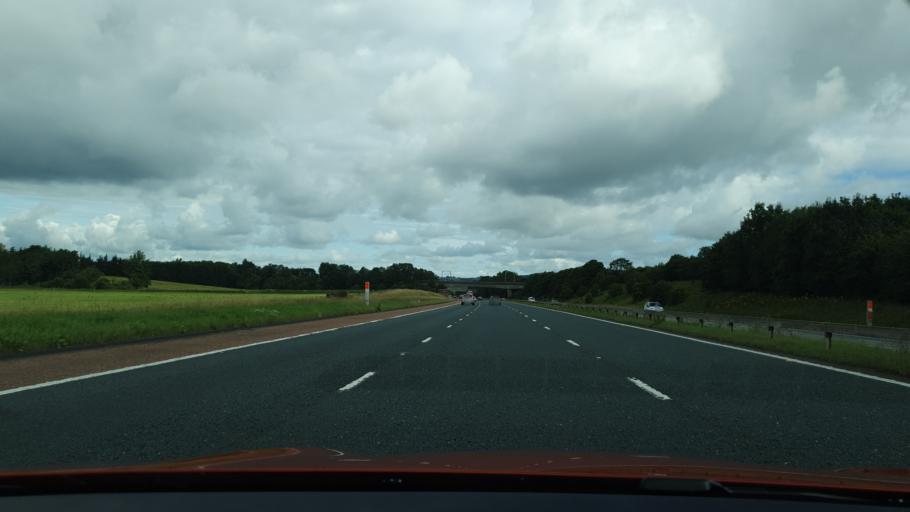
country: GB
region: England
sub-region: Cumbria
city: Penrith
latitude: 54.6308
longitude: -2.7253
